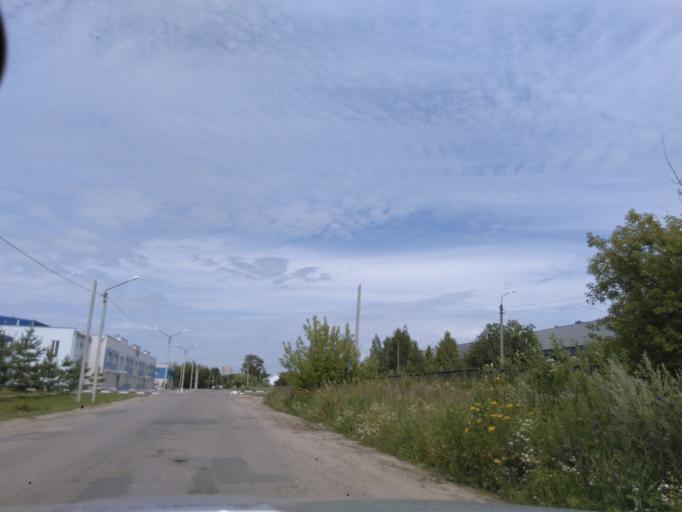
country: RU
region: Moskovskaya
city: Solnechnogorsk
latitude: 56.1684
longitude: 36.9788
